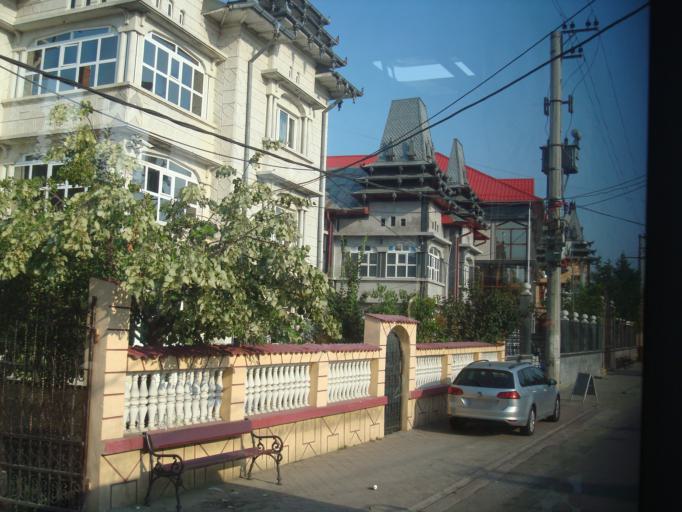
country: RO
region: Ilfov
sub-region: Comuna Vidra
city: Sintesti
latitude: 44.3164
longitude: 26.1063
